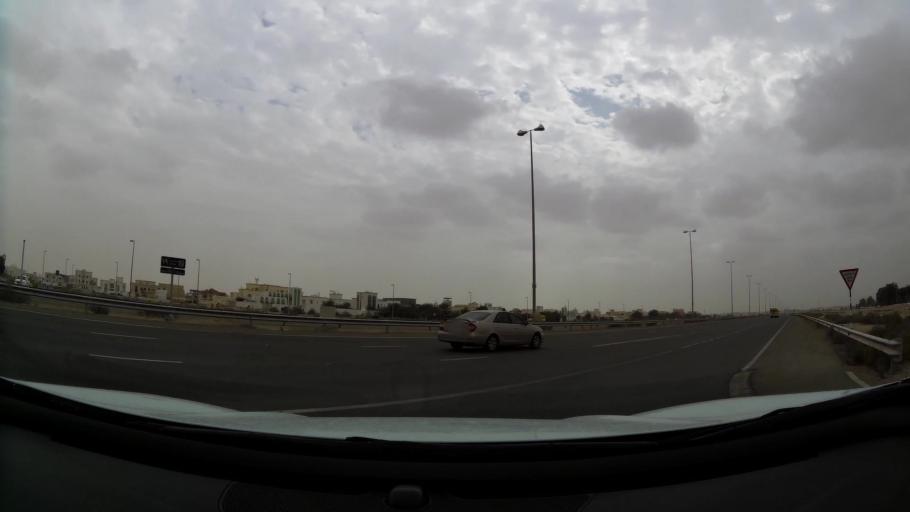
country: AE
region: Abu Dhabi
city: Abu Dhabi
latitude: 24.3439
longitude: 54.6477
